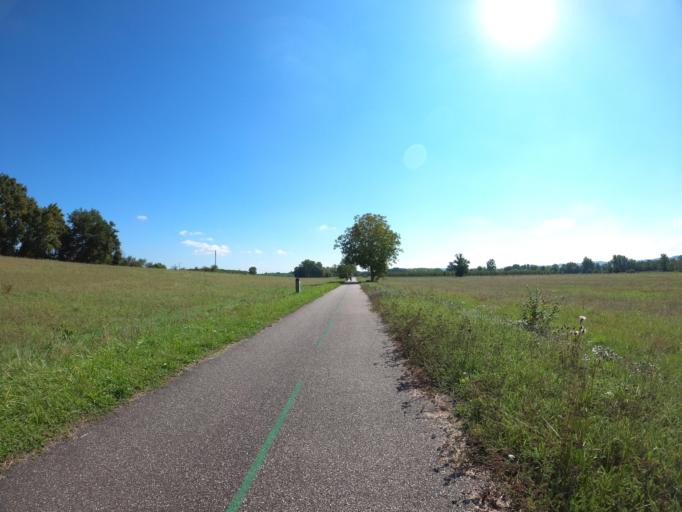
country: FR
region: Aquitaine
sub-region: Departement du Lot-et-Garonne
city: Bias
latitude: 44.4268
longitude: 0.6461
